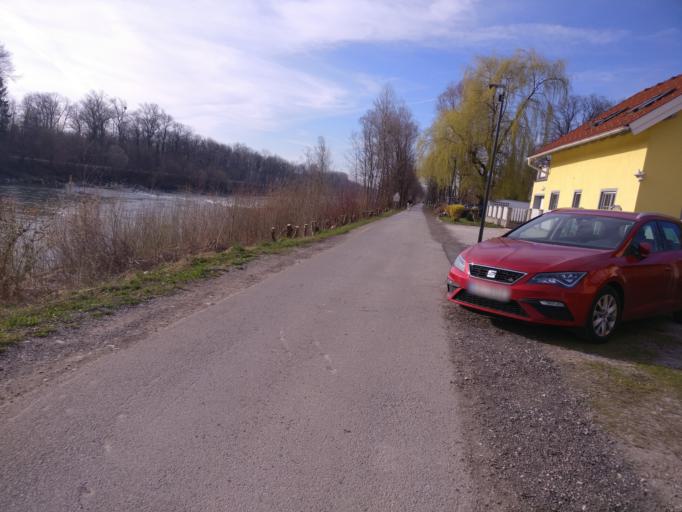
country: AT
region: Salzburg
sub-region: Politischer Bezirk Salzburg-Umgebung
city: Bergheim
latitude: 47.8349
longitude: 13.0252
